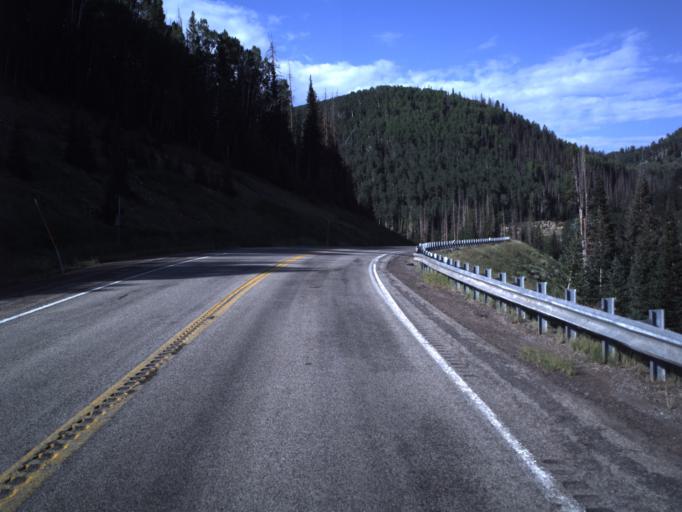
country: US
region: Utah
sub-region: Sanpete County
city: Fairview
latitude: 39.6001
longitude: -111.2172
